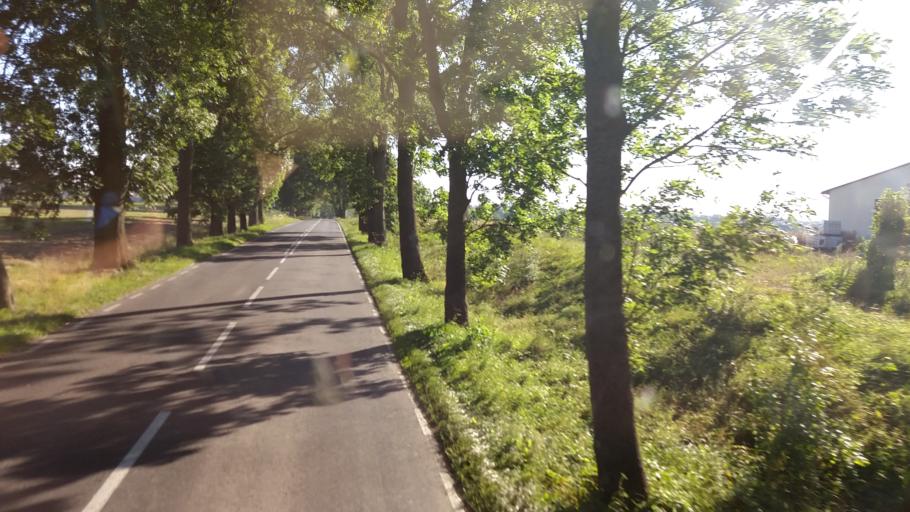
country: PL
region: West Pomeranian Voivodeship
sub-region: Powiat choszczenski
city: Choszczno
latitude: 53.1837
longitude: 15.4266
